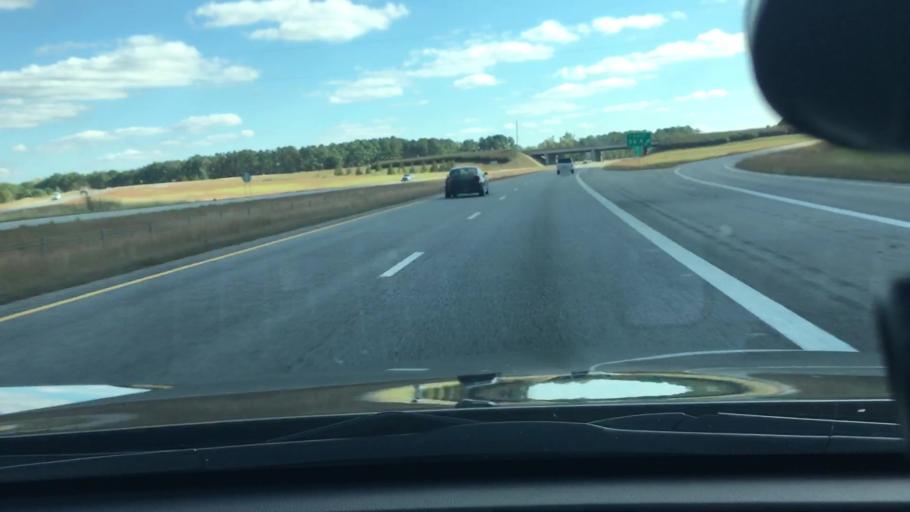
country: US
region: North Carolina
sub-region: Wilson County
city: Lucama
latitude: 35.7649
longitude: -78.0316
